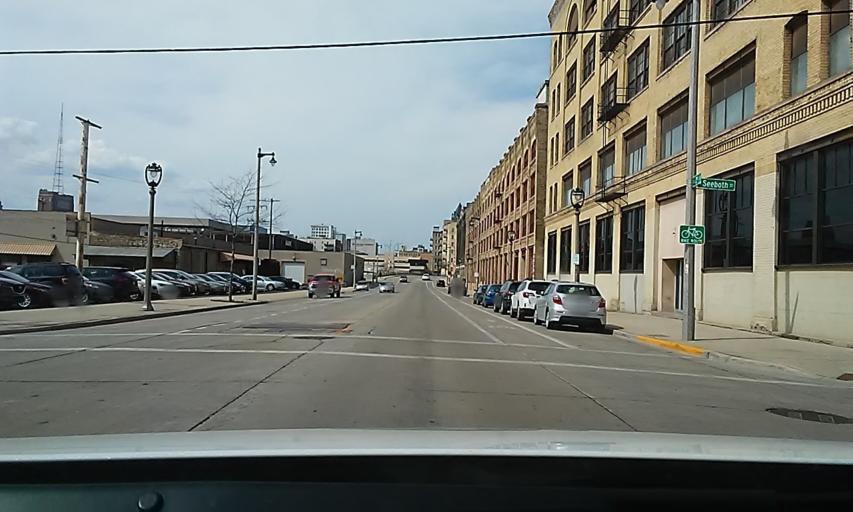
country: US
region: Wisconsin
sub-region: Milwaukee County
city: Milwaukee
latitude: 43.0304
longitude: -87.9126
